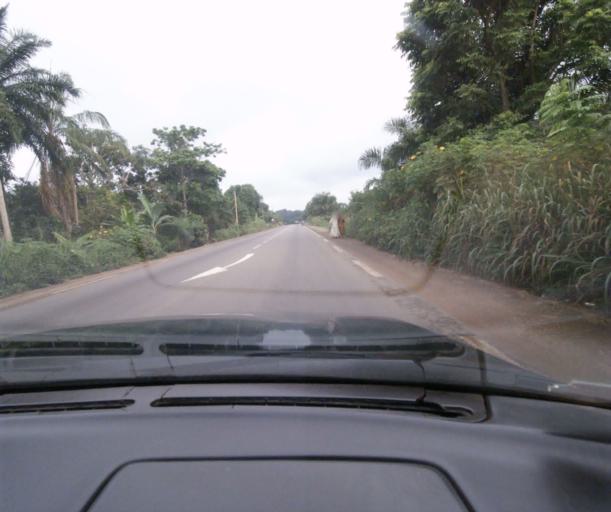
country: CM
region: Centre
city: Obala
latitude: 4.1643
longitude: 11.4997
